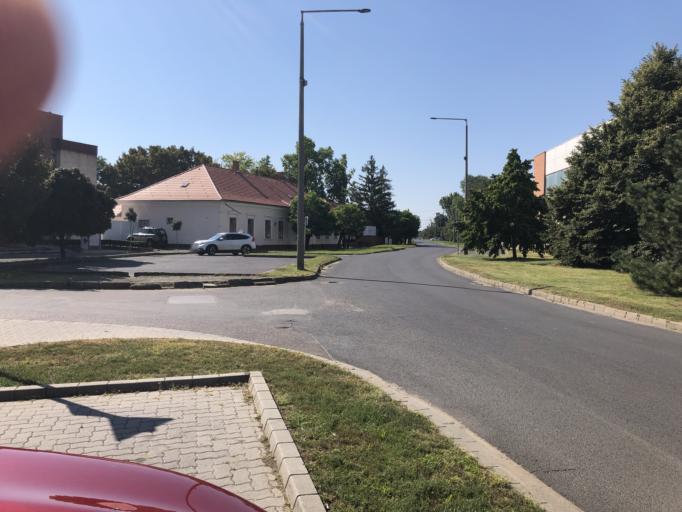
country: HU
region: Jasz-Nagykun-Szolnok
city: Kisujszallas
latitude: 47.2181
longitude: 20.7606
